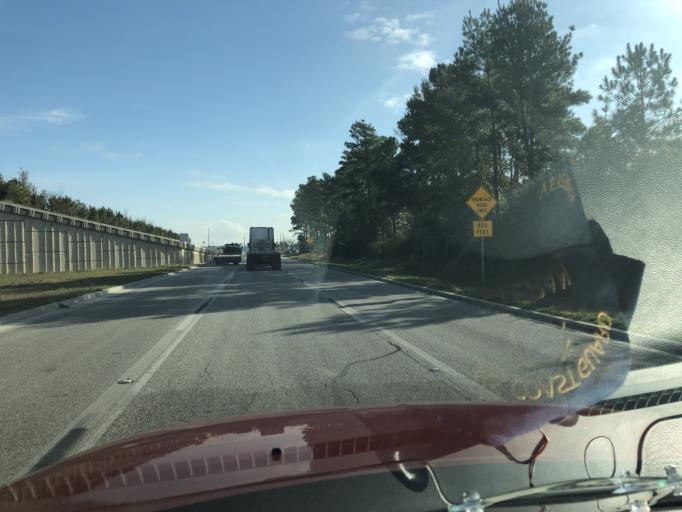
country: US
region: Texas
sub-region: Harris County
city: Tomball
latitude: 30.0514
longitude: -95.6120
